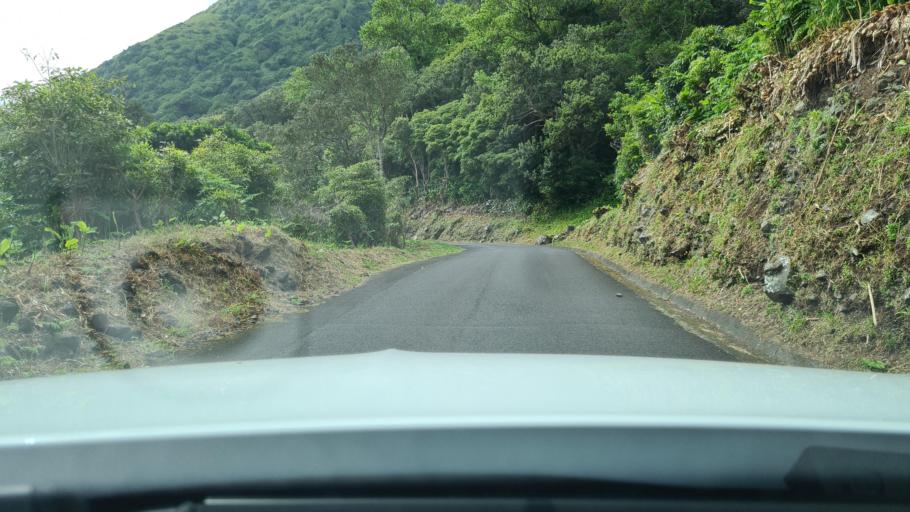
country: PT
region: Azores
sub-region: Sao Roque do Pico
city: Sao Roque do Pico
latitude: 38.6394
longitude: -27.9679
